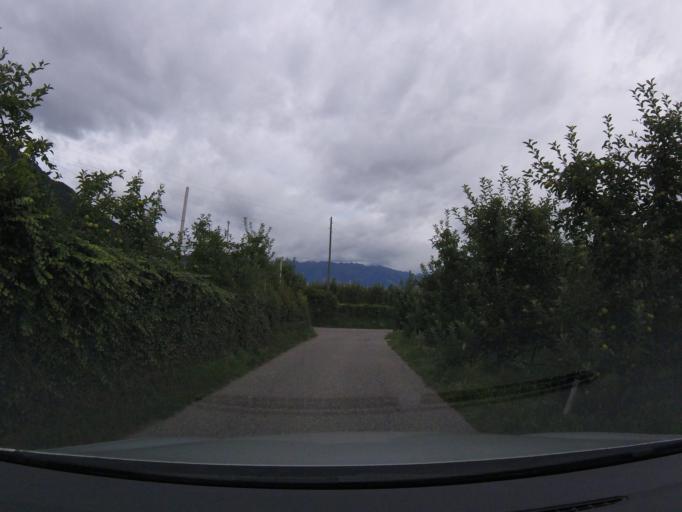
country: IT
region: Trentino-Alto Adige
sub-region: Bolzano
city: Tesimo
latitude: 46.5510
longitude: 11.1792
